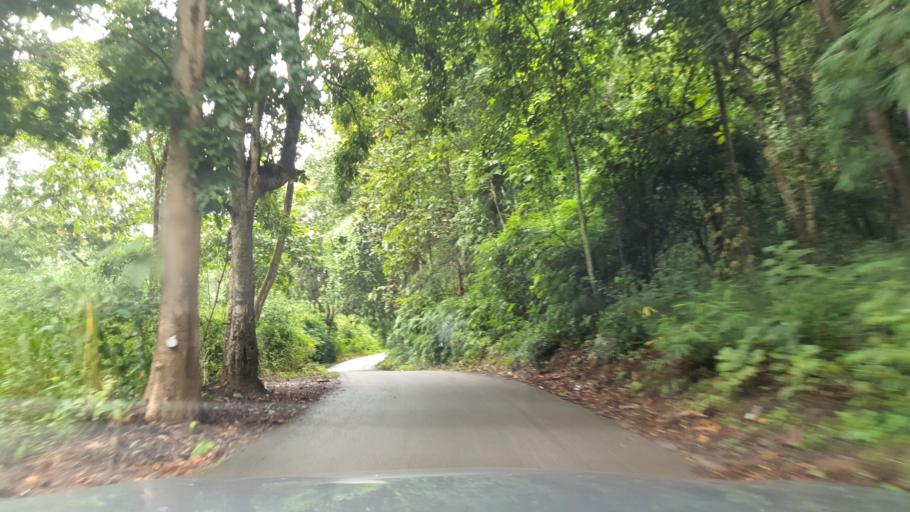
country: TH
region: Chiang Mai
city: Mae Taeng
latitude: 19.2069
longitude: 98.9322
